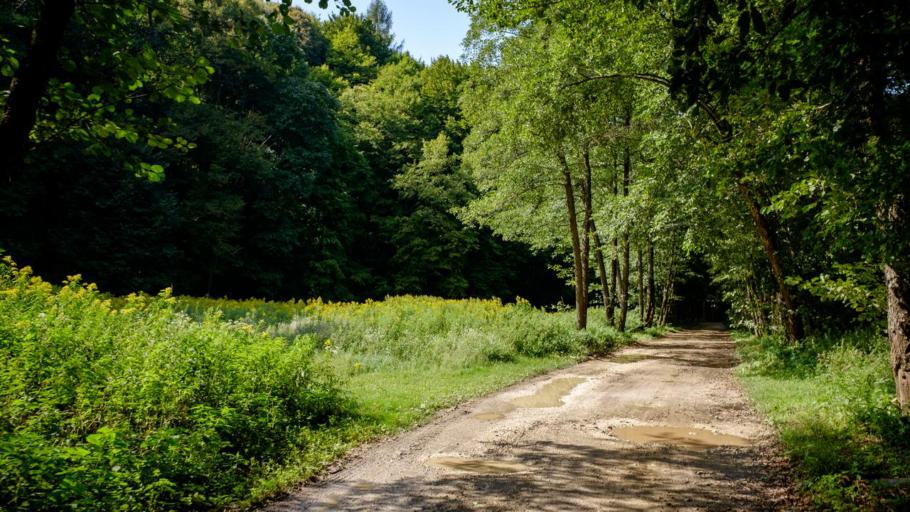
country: HU
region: Gyor-Moson-Sopron
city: Bakonyszentlaszlo
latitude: 47.3362
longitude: 17.8163
